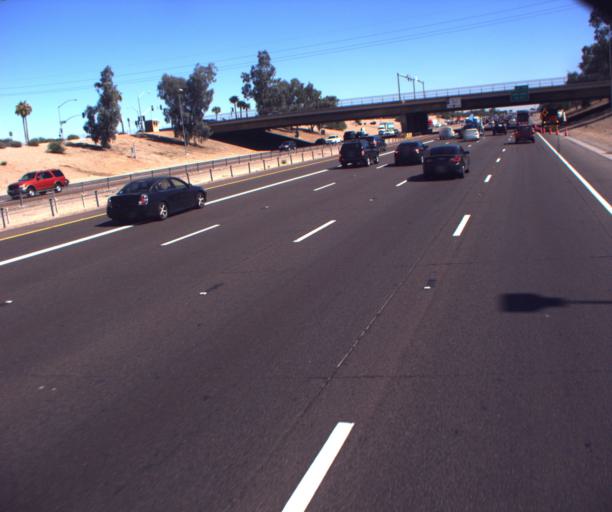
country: US
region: Arizona
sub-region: Maricopa County
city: Tolleson
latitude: 33.4626
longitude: -112.1881
